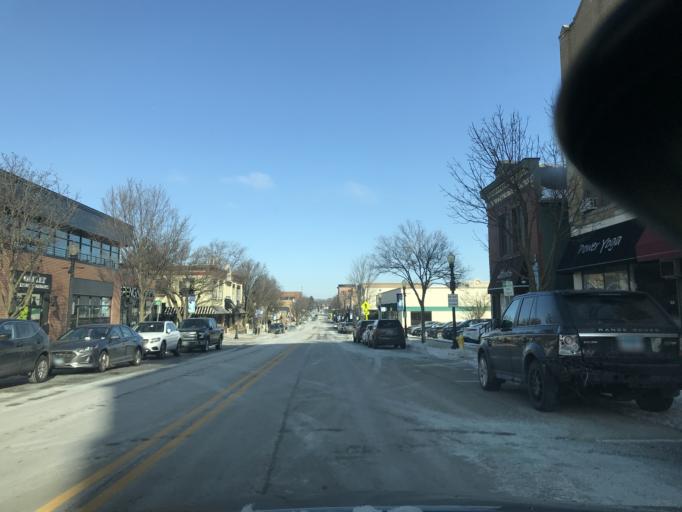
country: US
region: Illinois
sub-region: DuPage County
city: Downers Grove
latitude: 41.7918
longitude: -88.0101
